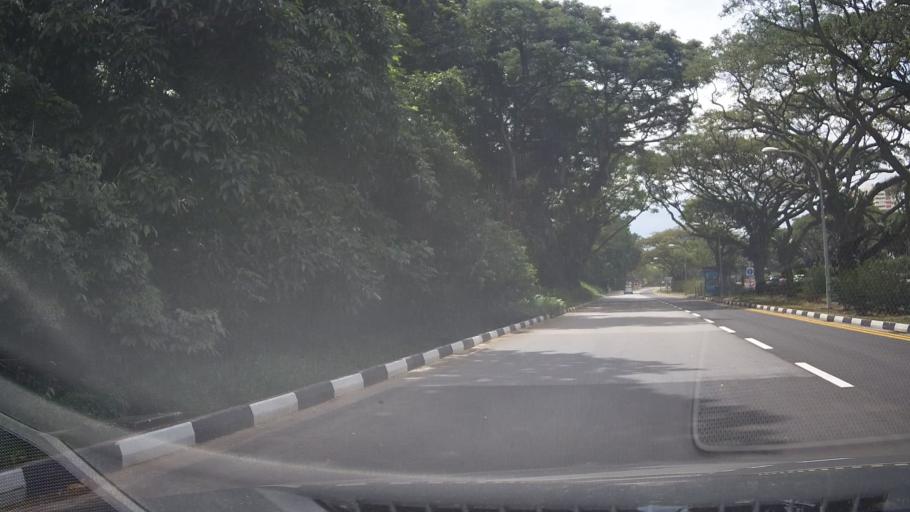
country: SG
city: Singapore
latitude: 1.3068
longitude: 103.9286
